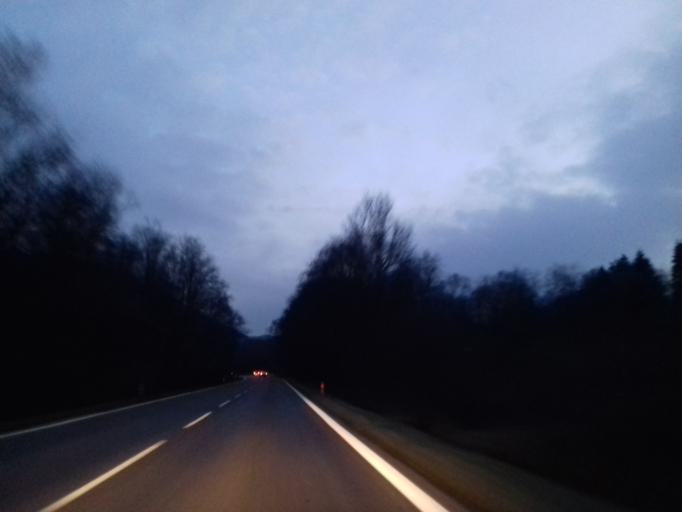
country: SK
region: Zilinsky
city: Ruzomberok
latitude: 48.9735
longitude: 19.2732
